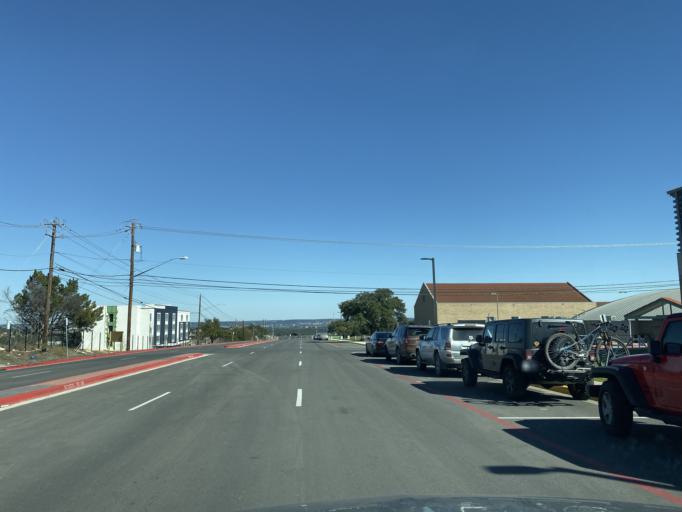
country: US
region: Texas
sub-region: Travis County
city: The Hills
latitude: 30.3284
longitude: -97.9696
